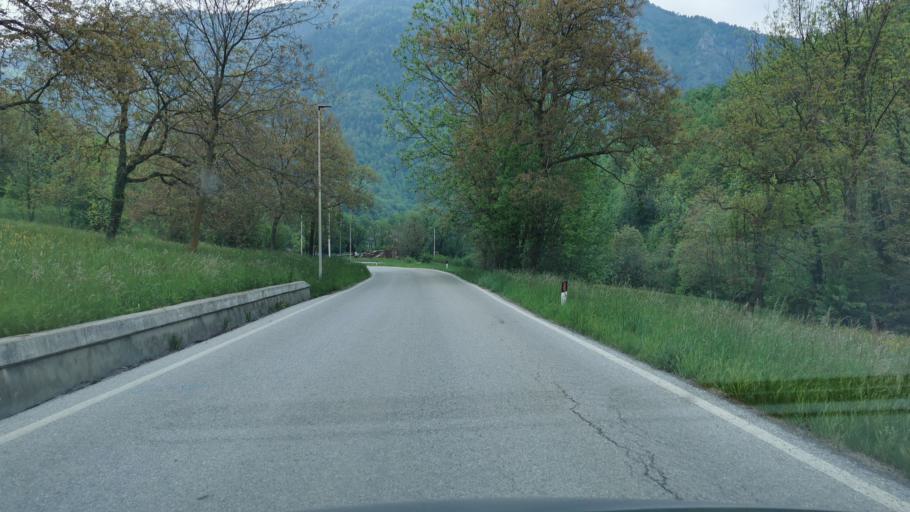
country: IT
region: Piedmont
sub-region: Provincia di Cuneo
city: Monterosso Grana
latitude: 44.4042
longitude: 7.3113
